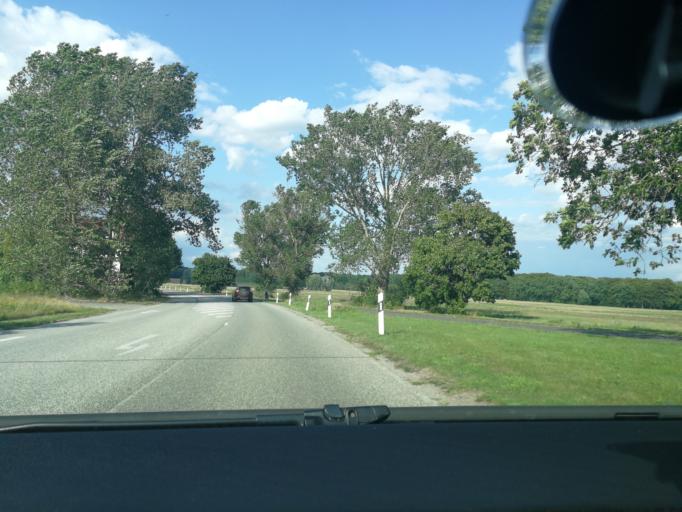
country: DE
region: Brandenburg
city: Pritzwalk
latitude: 53.1613
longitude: 12.1820
